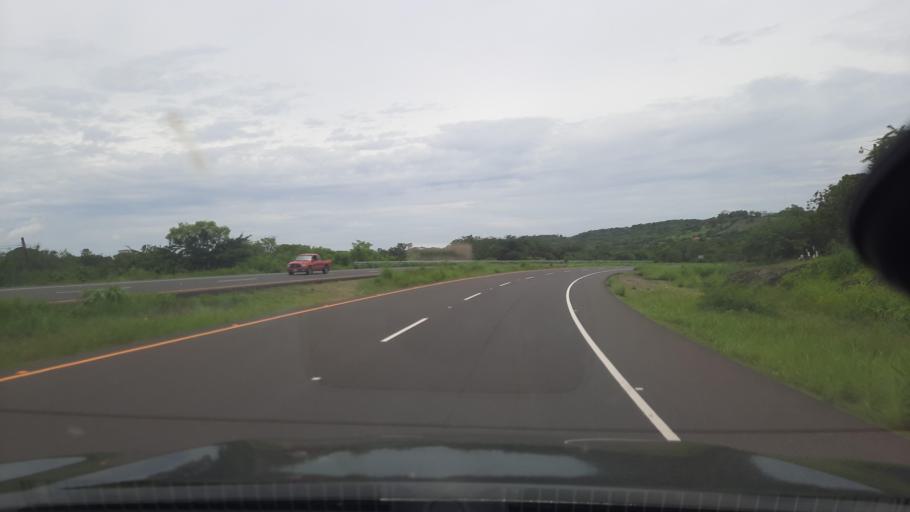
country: HN
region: Valle
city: Aramecina
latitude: 13.7598
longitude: -87.7091
